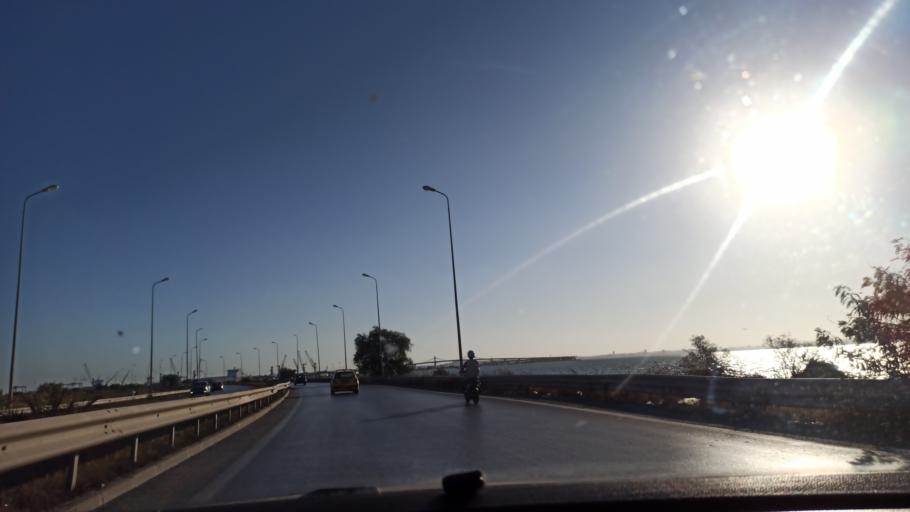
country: TN
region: Tunis
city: La Goulette
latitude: 36.8163
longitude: 10.2830
